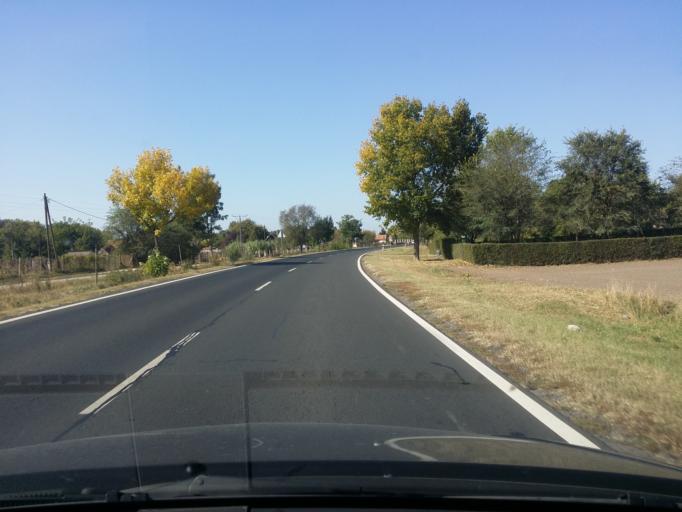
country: HU
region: Bacs-Kiskun
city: Nyarlorinc
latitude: 46.8693
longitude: 19.8574
